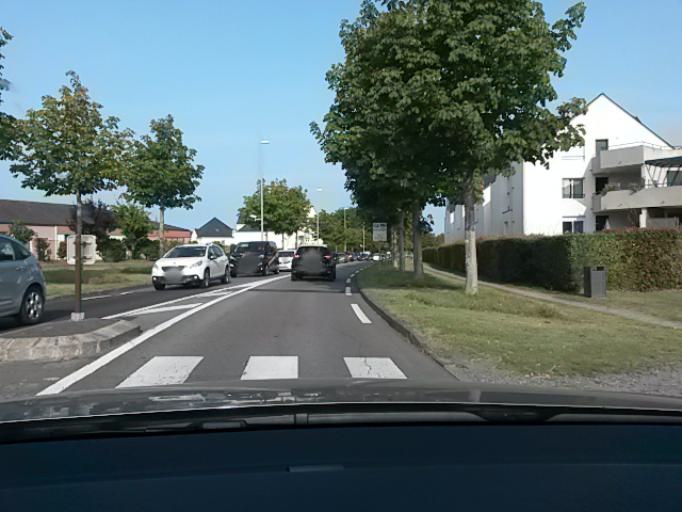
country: FR
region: Pays de la Loire
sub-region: Departement de la Loire-Atlantique
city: Guerande
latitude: 47.3274
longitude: -2.4177
